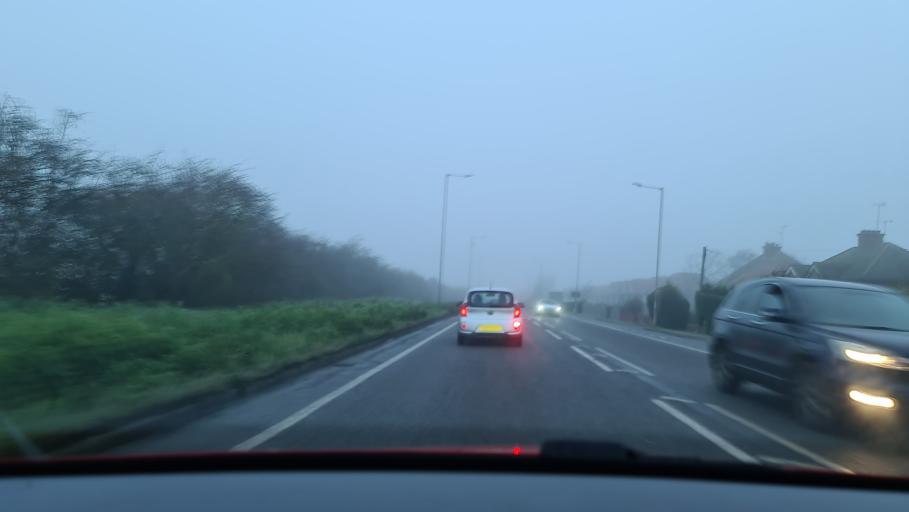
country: GB
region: England
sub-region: Buckinghamshire
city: Weston Turville
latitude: 51.8073
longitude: -0.7568
